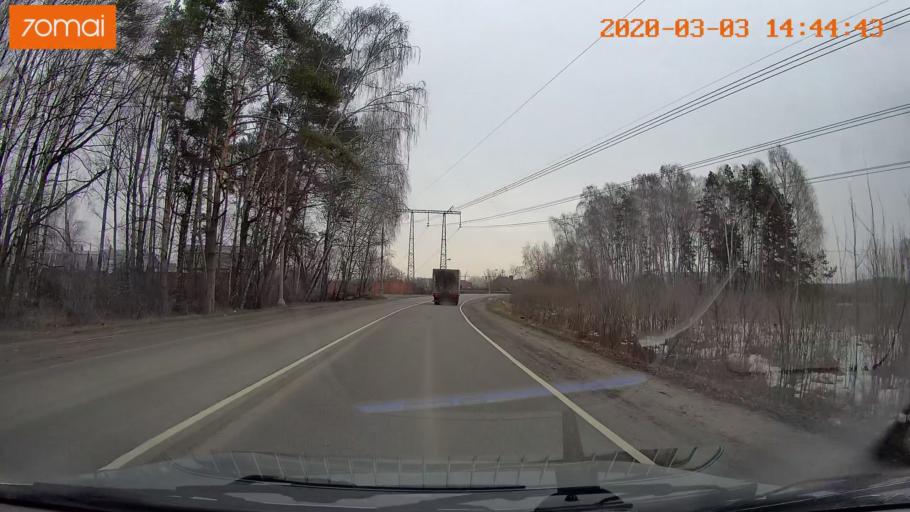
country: RU
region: Moskovskaya
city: Korenevo
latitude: 55.7018
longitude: 38.0355
